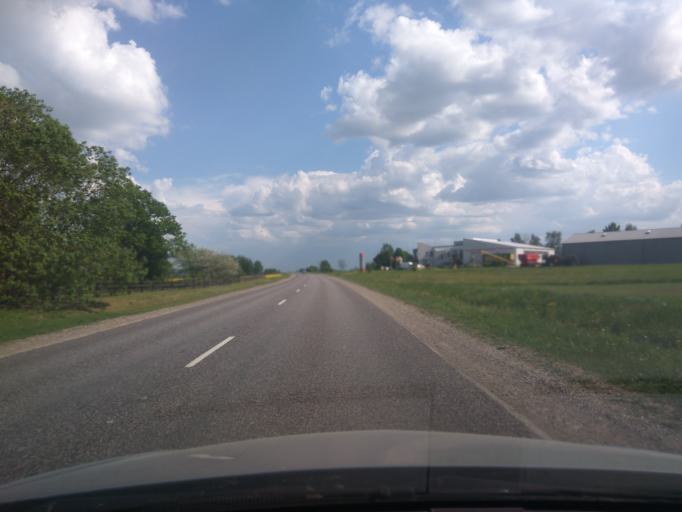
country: LV
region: Kuldigas Rajons
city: Kuldiga
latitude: 56.9997
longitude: 21.8984
